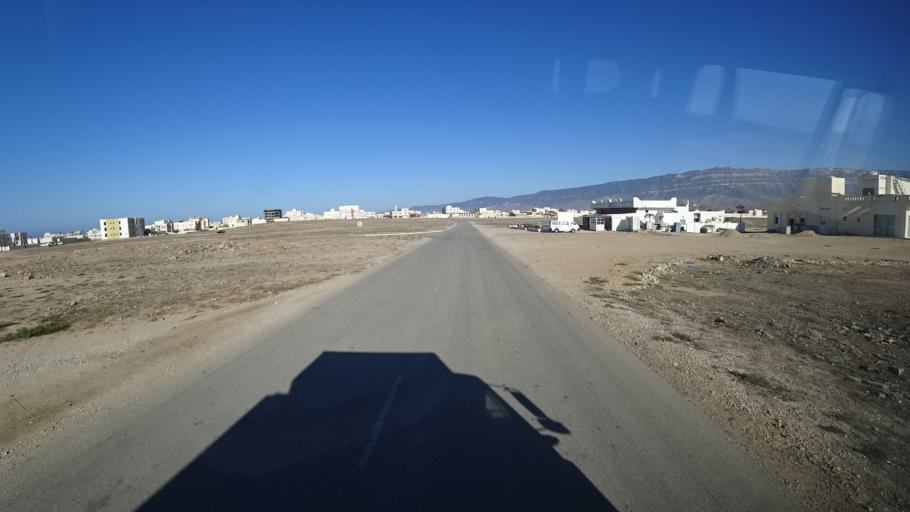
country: OM
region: Zufar
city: Salalah
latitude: 16.9804
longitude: 54.6972
